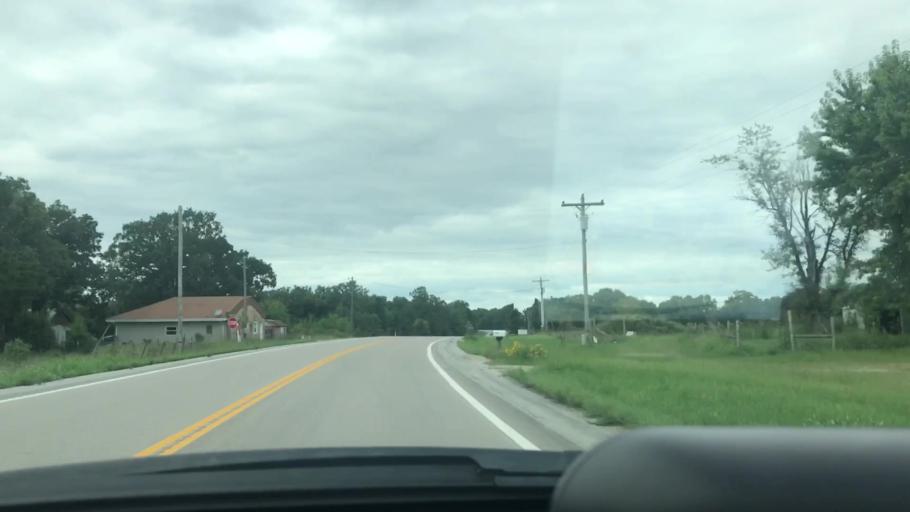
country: US
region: Missouri
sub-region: Benton County
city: Warsaw
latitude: 38.1543
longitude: -93.2962
